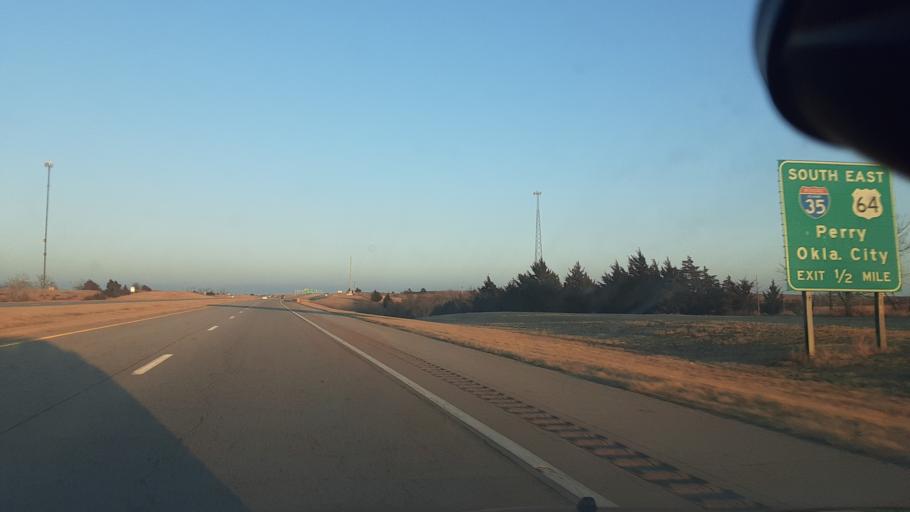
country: US
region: Oklahoma
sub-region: Noble County
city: Perry
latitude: 36.3994
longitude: -97.3426
